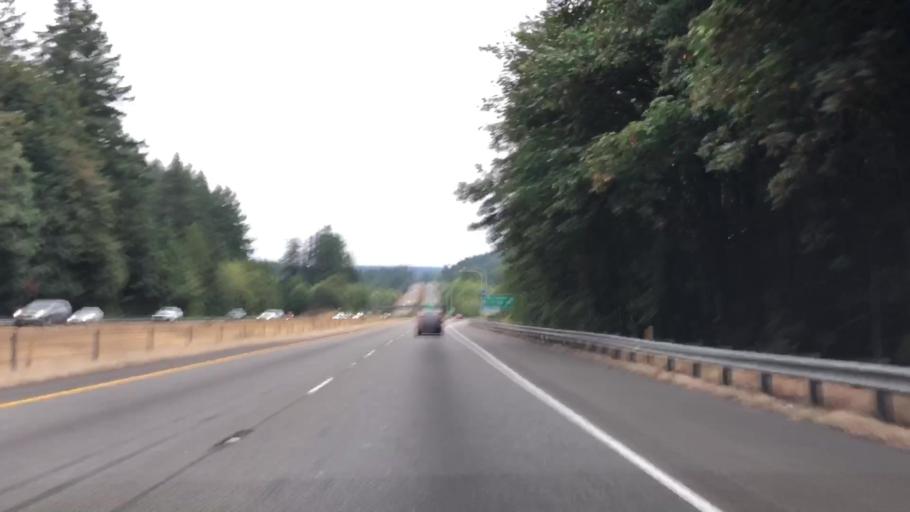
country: US
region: Washington
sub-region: Pierce County
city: Canterwood
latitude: 47.3535
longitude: -122.6121
